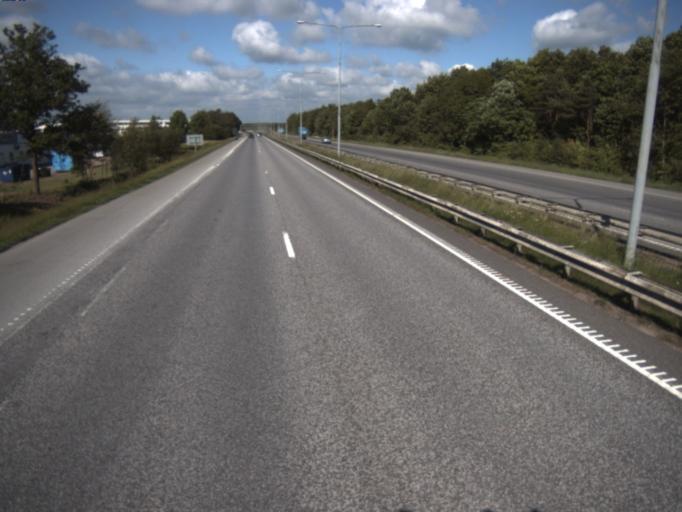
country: SE
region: Skane
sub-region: Helsingborg
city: Odakra
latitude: 56.0705
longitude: 12.7251
